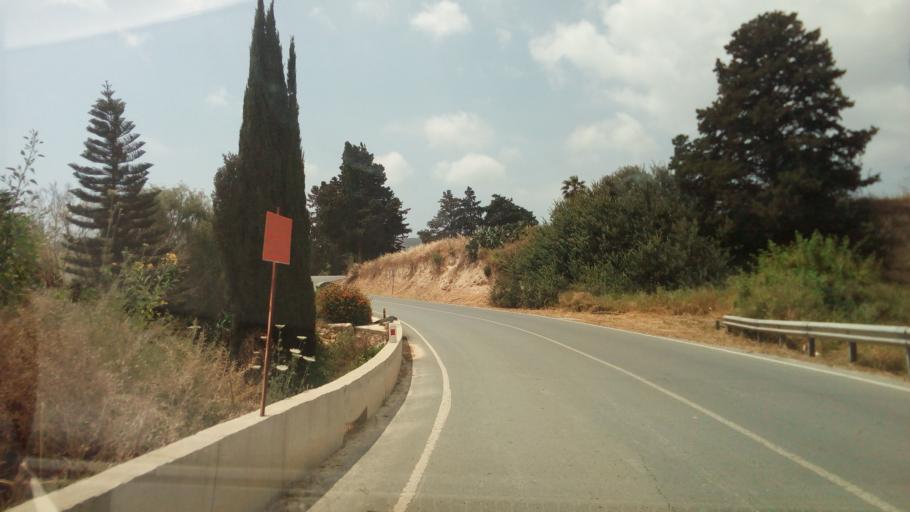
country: CY
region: Limassol
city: Pissouri
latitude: 34.6762
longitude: 32.7221
